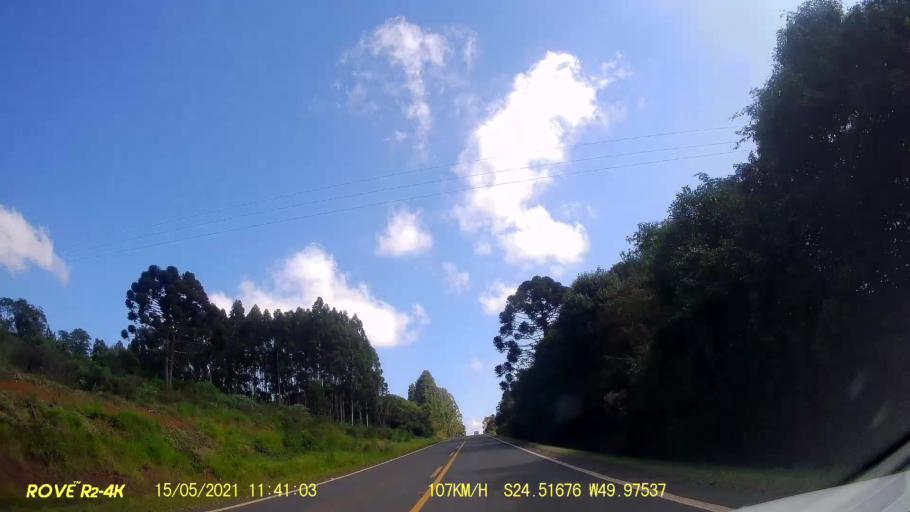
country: BR
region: Parana
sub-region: Pirai Do Sul
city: Pirai do Sul
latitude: -24.5168
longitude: -49.9752
